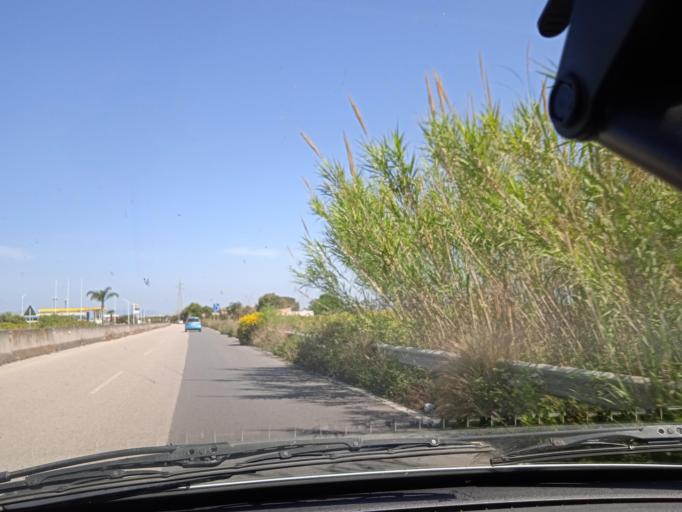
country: IT
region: Sicily
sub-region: Messina
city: San Filippo del Mela
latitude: 38.1912
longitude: 15.2602
